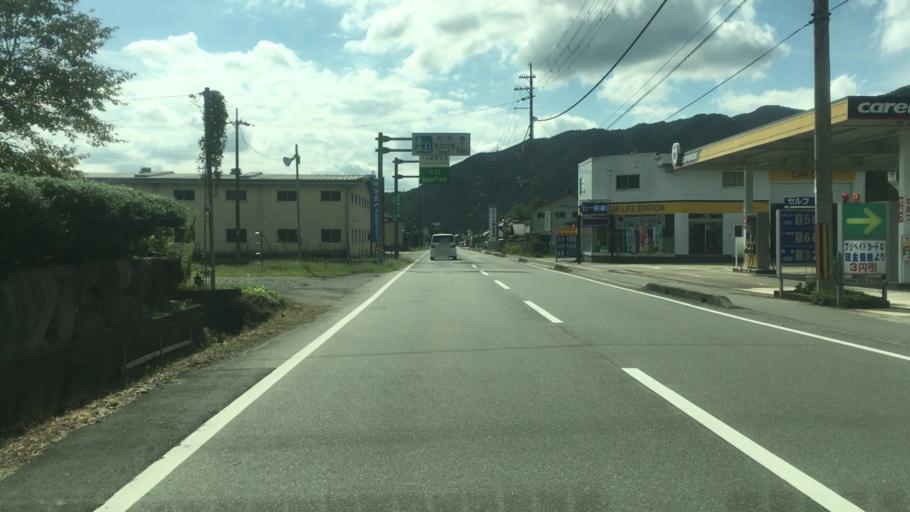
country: JP
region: Kyoto
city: Fukuchiyama
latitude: 35.2458
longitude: 135.0070
